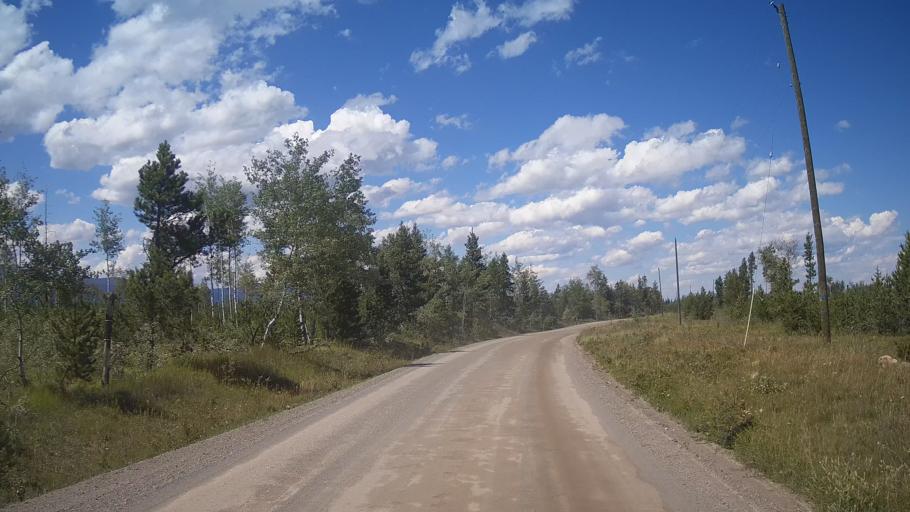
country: CA
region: British Columbia
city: Cache Creek
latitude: 51.2516
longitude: -121.6719
